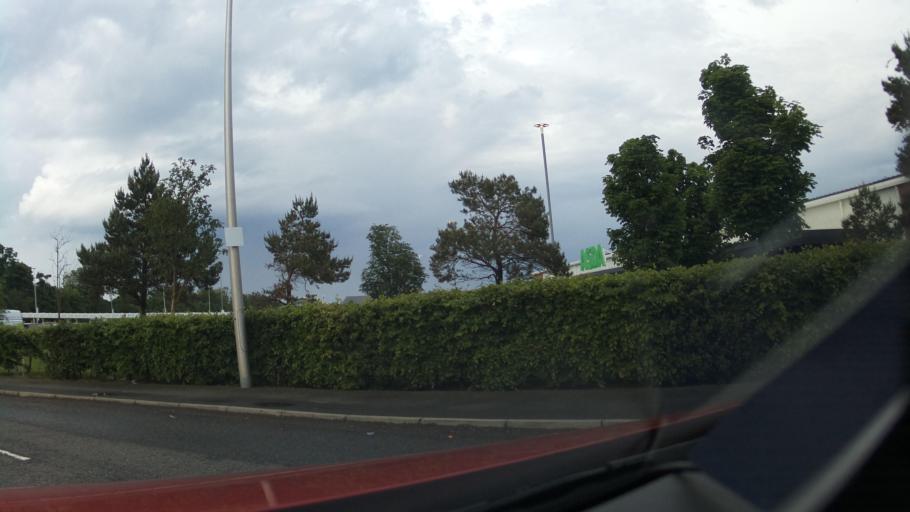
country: GB
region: Scotland
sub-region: East Lothian
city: Dunbar
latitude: 55.9889
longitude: -2.5113
